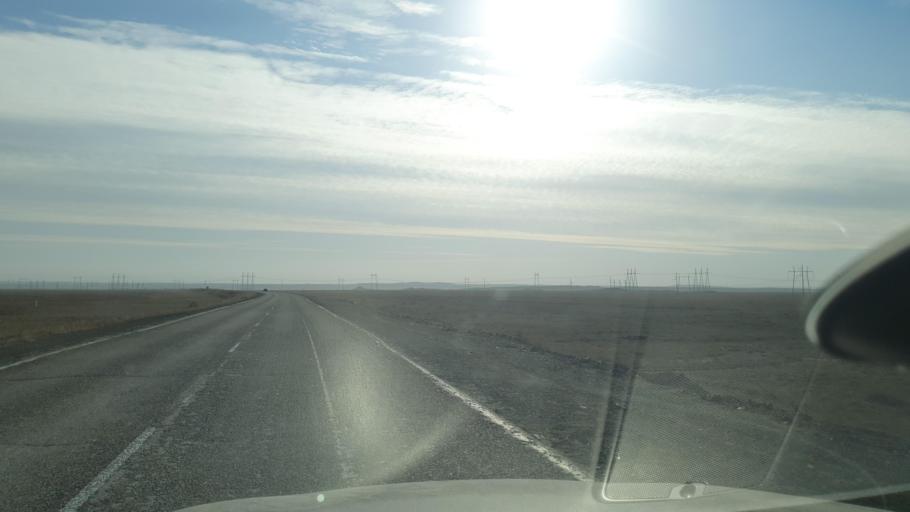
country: KZ
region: Zhambyl
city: Mynaral
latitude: 45.6140
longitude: 73.3960
